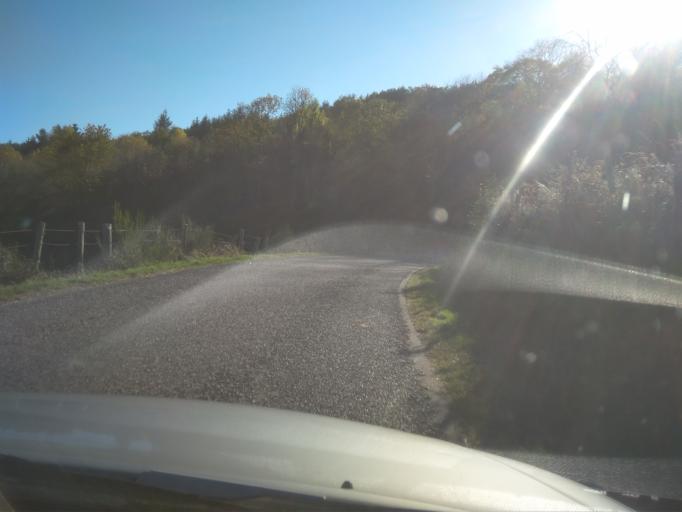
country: FR
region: Rhone-Alpes
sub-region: Departement de la Loire
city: Ambierle
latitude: 46.1214
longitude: 3.8599
